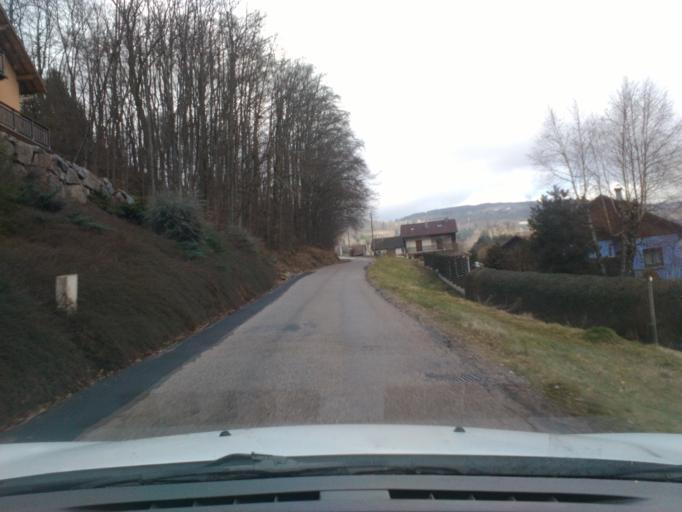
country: FR
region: Lorraine
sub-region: Departement des Vosges
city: Cornimont
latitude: 47.9659
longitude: 6.8306
